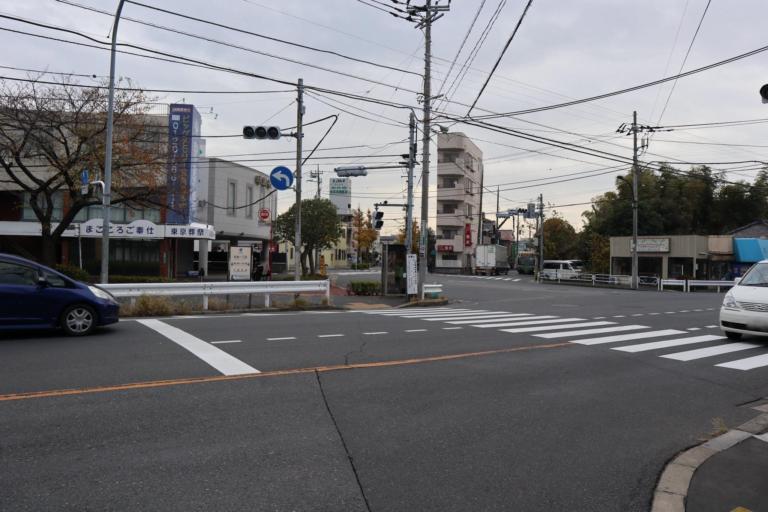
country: JP
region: Tokyo
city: Urayasu
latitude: 35.7161
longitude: 139.8741
